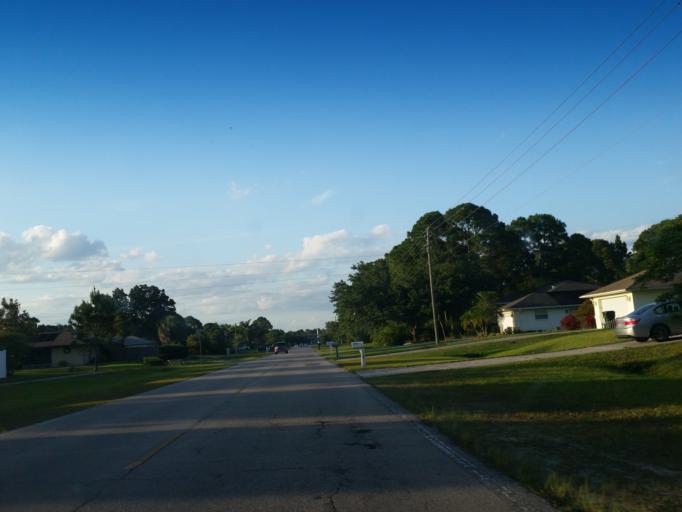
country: US
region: Florida
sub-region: Sarasota County
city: North Port
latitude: 27.0648
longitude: -82.1979
